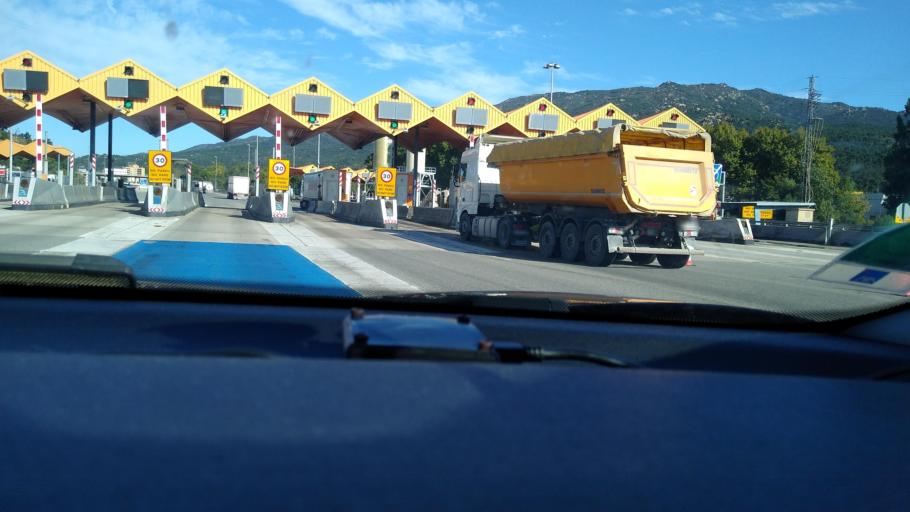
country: ES
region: Catalonia
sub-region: Provincia de Girona
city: la Jonquera
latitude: 42.4096
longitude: 2.8725
